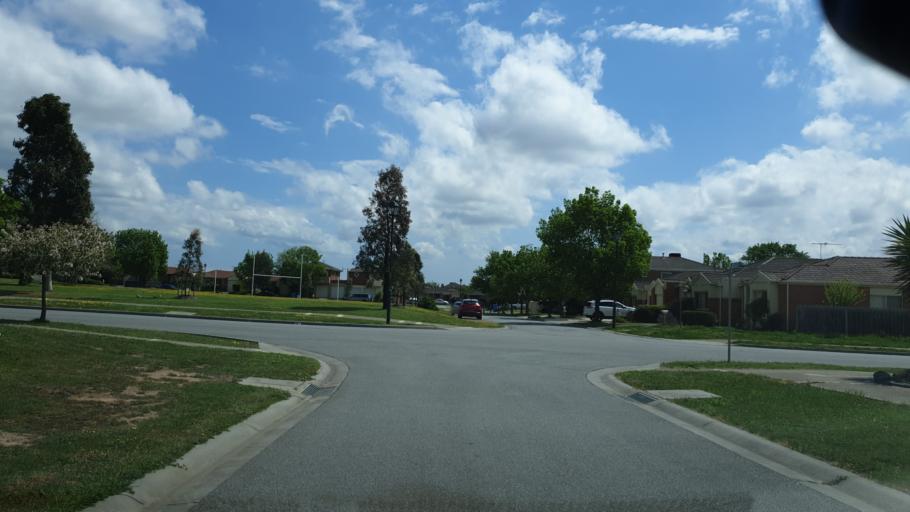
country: AU
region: Victoria
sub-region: Casey
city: Narre Warren South
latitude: -38.0658
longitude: 145.2932
